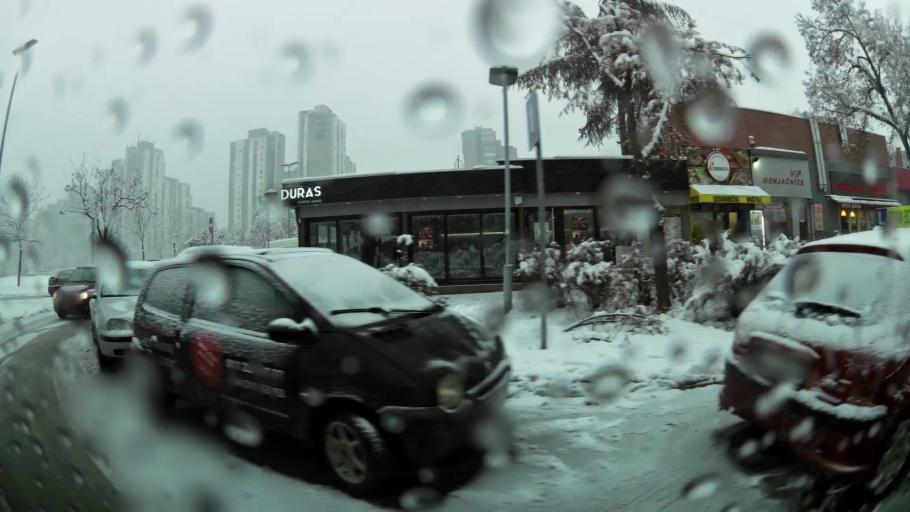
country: RS
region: Central Serbia
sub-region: Belgrade
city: Zemun
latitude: 44.8021
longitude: 20.3710
